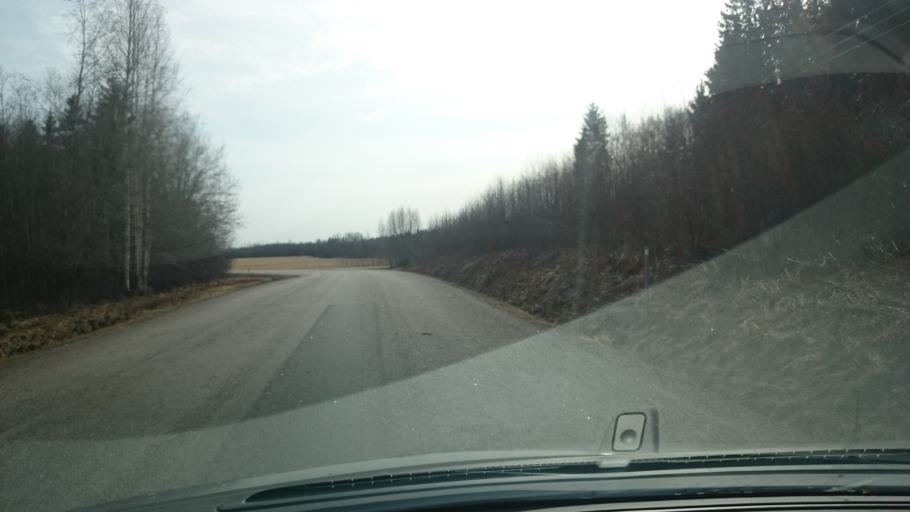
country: EE
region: Jaervamaa
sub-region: Tueri vald
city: Tueri
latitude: 58.9213
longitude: 25.4435
